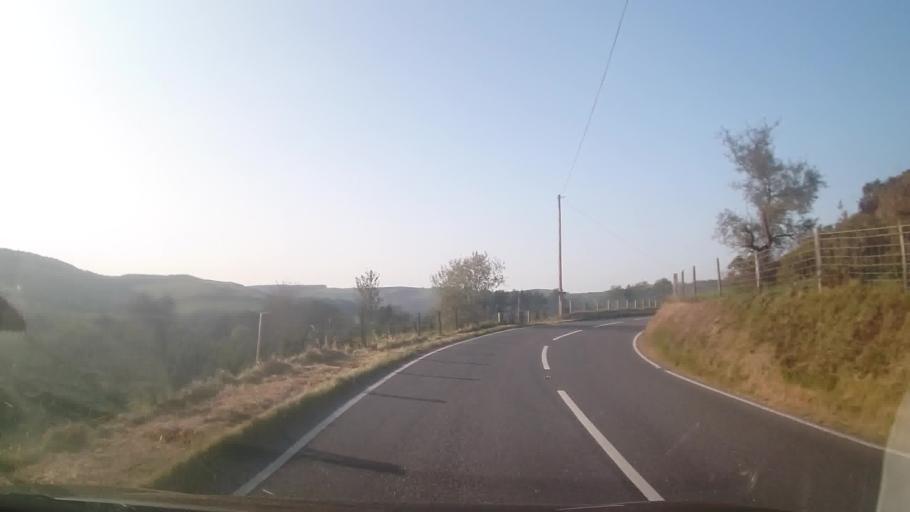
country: GB
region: Wales
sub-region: County of Ceredigion
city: Lledrod
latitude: 52.3226
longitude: -3.8603
